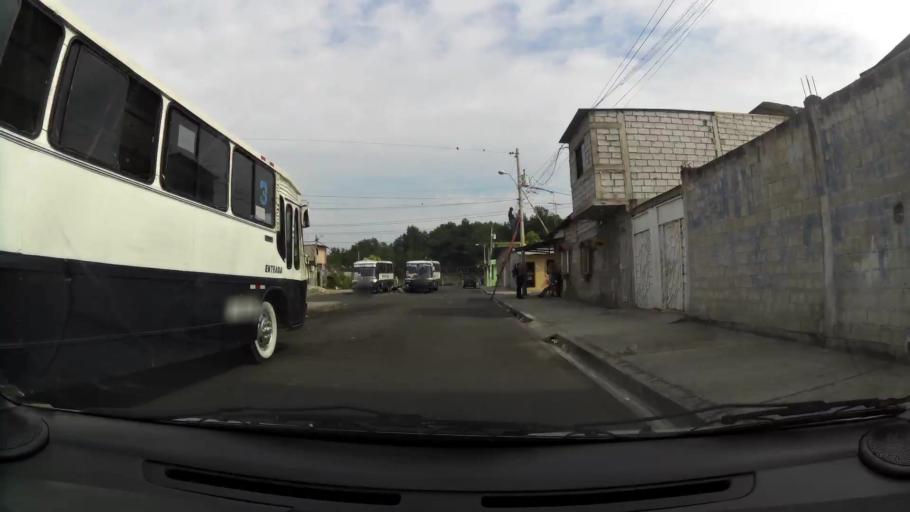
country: EC
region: Guayas
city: Guayaquil
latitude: -2.2602
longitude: -79.9033
